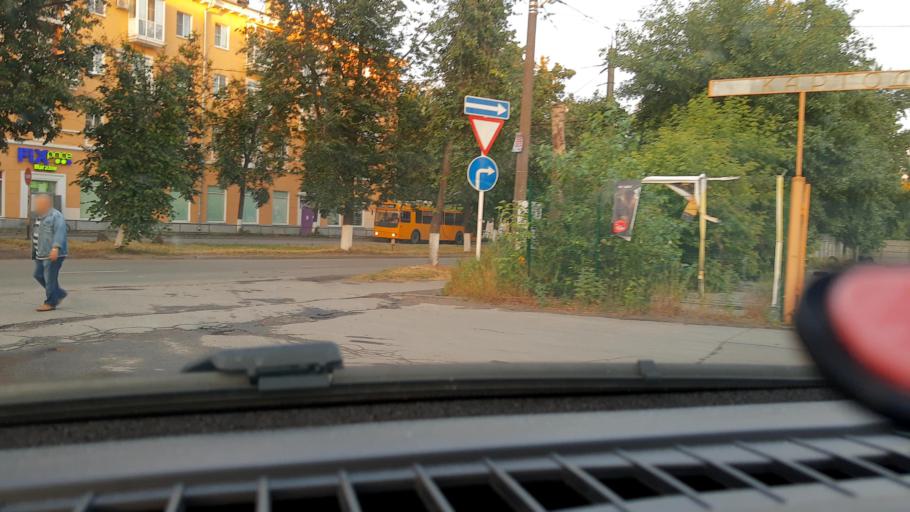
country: RU
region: Nizjnij Novgorod
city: Dzerzhinsk
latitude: 56.2383
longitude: 43.4764
